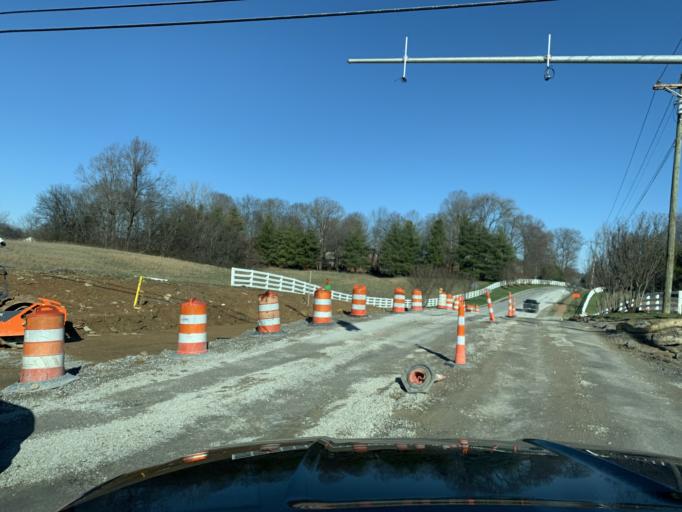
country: US
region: Tennessee
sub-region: Maury County
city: Spring Hill
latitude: 35.7526
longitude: -86.9021
